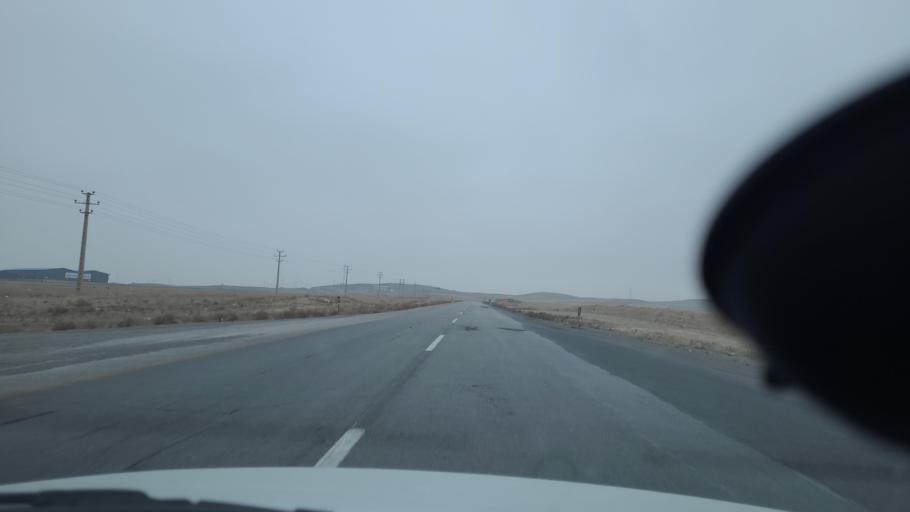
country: IR
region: Razavi Khorasan
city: Fariman
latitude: 36.0113
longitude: 59.7613
